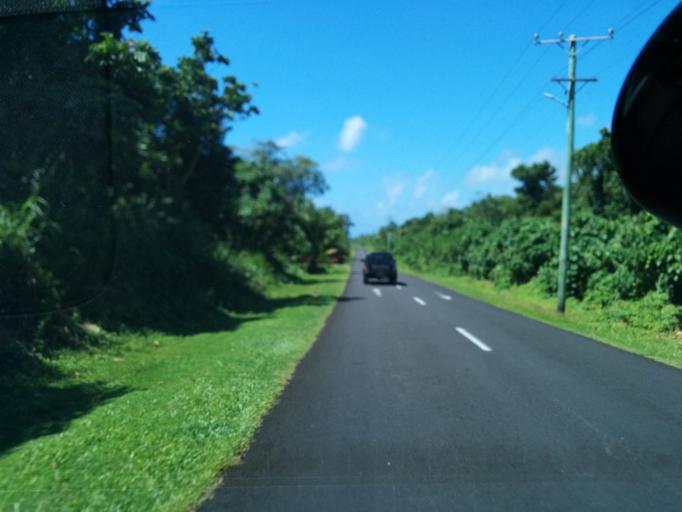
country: WS
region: Fa`asaleleaga
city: Safotulafai
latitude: -13.5376
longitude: -172.2511
